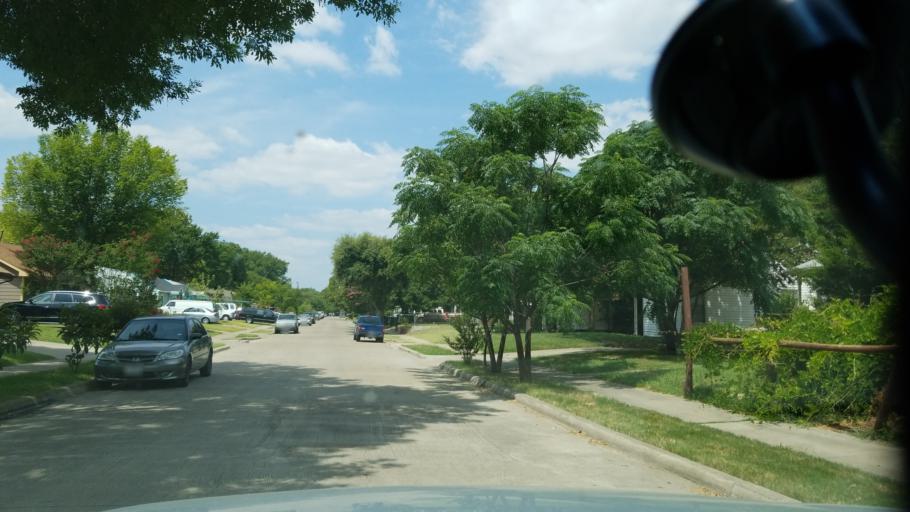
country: US
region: Texas
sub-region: Dallas County
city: Grand Prairie
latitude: 32.7529
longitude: -96.9819
